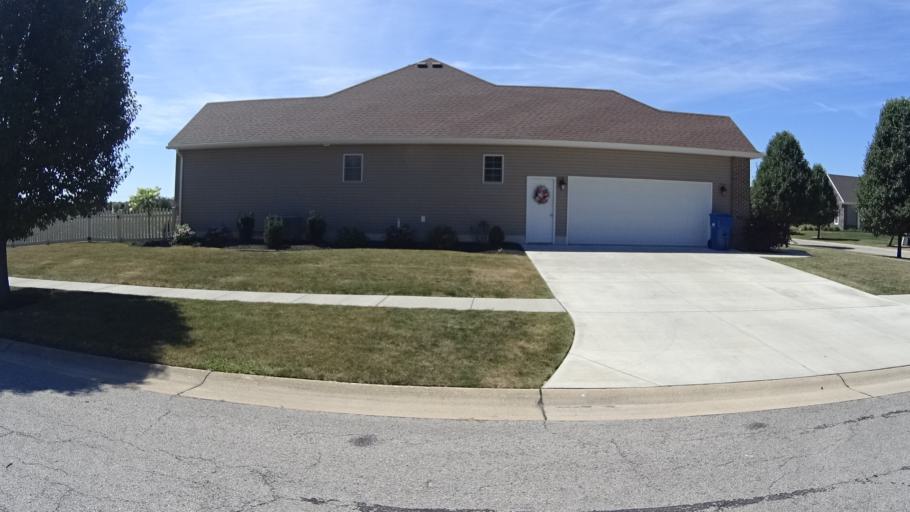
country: US
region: Ohio
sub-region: Erie County
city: Sandusky
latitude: 41.4075
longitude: -82.6981
